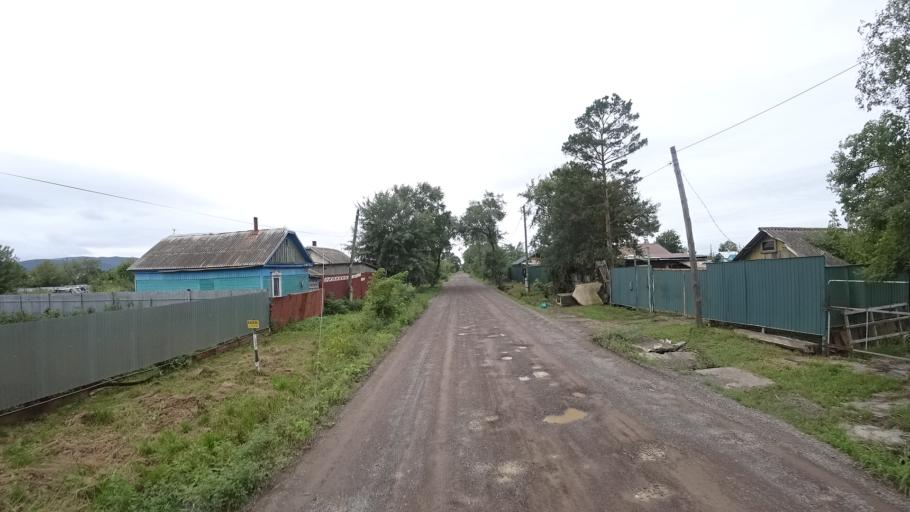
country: RU
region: Primorskiy
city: Chernigovka
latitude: 44.3392
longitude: 132.5669
